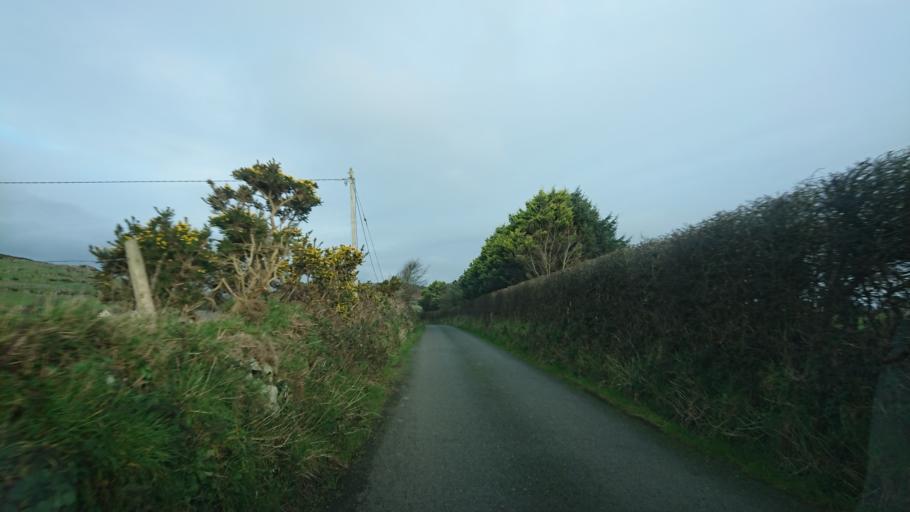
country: IE
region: Munster
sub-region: Waterford
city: Tra Mhor
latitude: 52.1605
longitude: -7.2149
